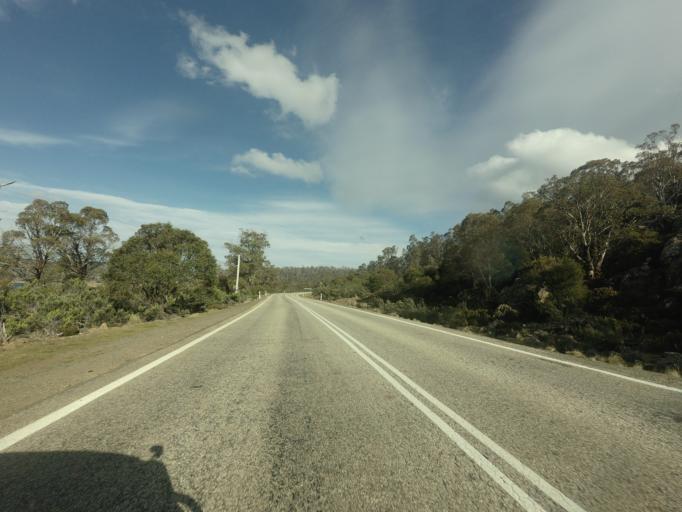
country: AU
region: Tasmania
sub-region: Meander Valley
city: Deloraine
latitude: -41.9827
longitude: 146.6790
